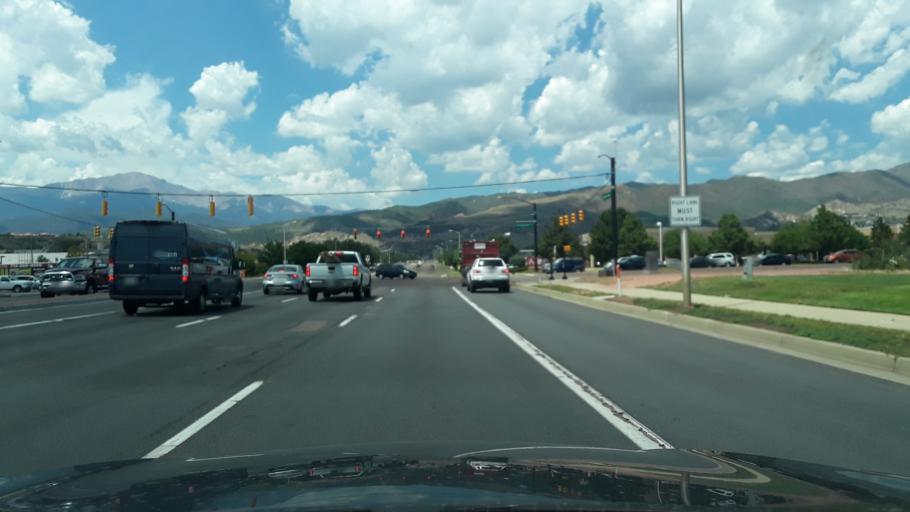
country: US
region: Colorado
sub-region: El Paso County
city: Colorado Springs
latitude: 38.8968
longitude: -104.8501
